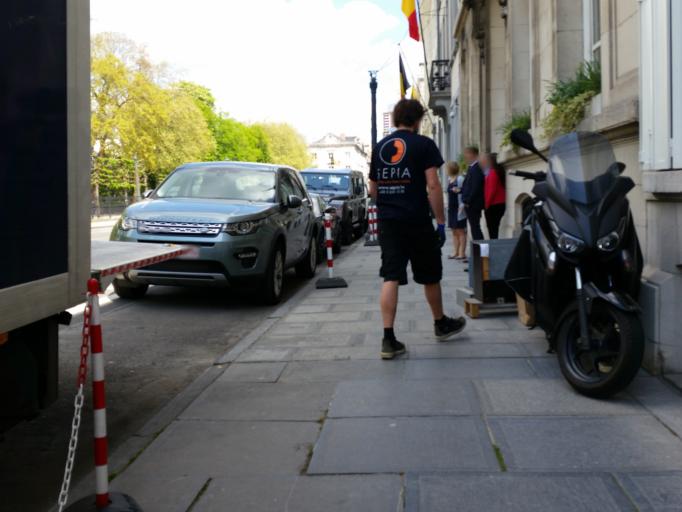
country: BE
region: Brussels Capital
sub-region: Bruxelles-Capitale
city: Brussels
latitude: 50.8438
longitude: 4.3658
